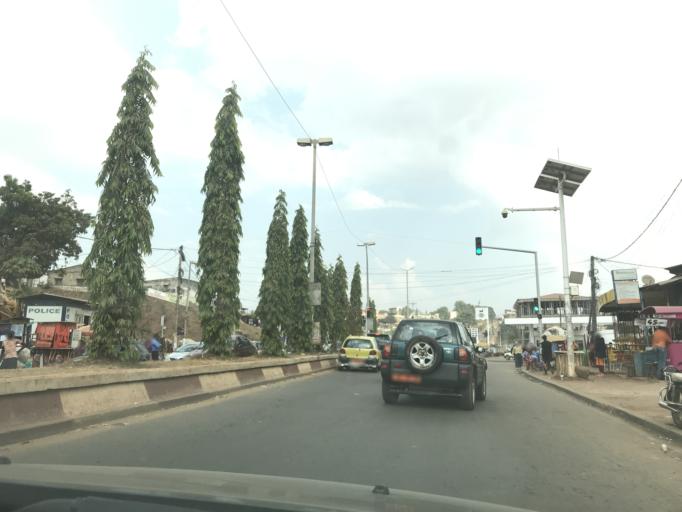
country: CM
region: Centre
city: Yaounde
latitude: 3.8869
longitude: 11.5299
